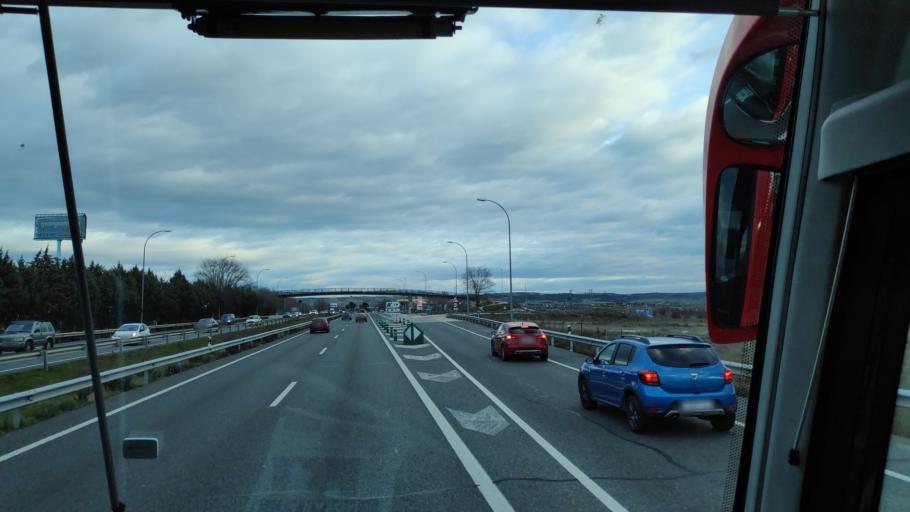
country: ES
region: Madrid
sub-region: Provincia de Madrid
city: Vaciamadrid
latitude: 40.3281
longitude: -3.5229
